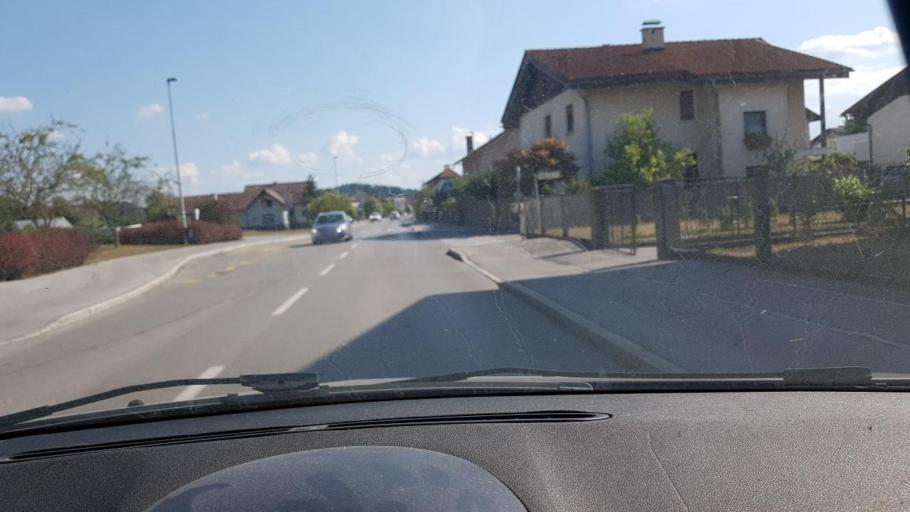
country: SI
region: Domzale
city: Vir
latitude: 46.1564
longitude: 14.6053
